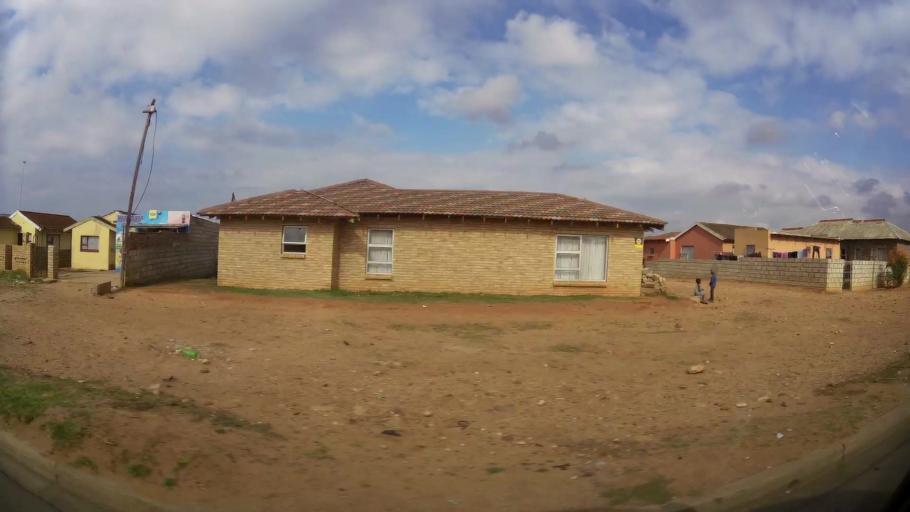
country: ZA
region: Eastern Cape
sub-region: Nelson Mandela Bay Metropolitan Municipality
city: Port Elizabeth
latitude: -33.8161
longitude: 25.5849
